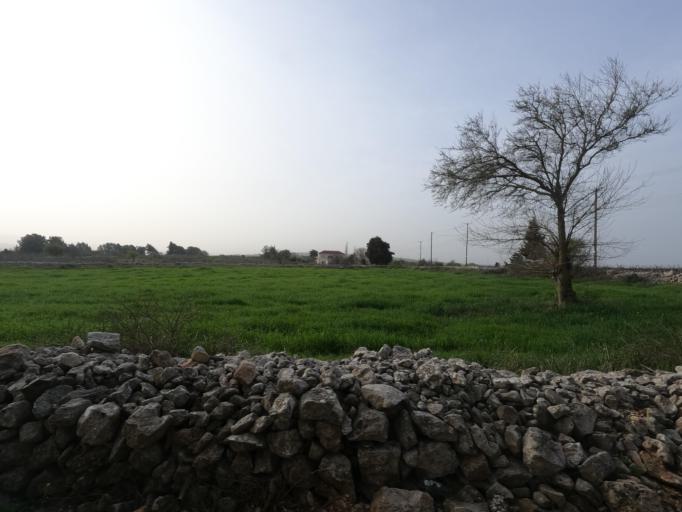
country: CY
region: Pafos
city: Pegeia
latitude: 34.9571
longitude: 32.4019
